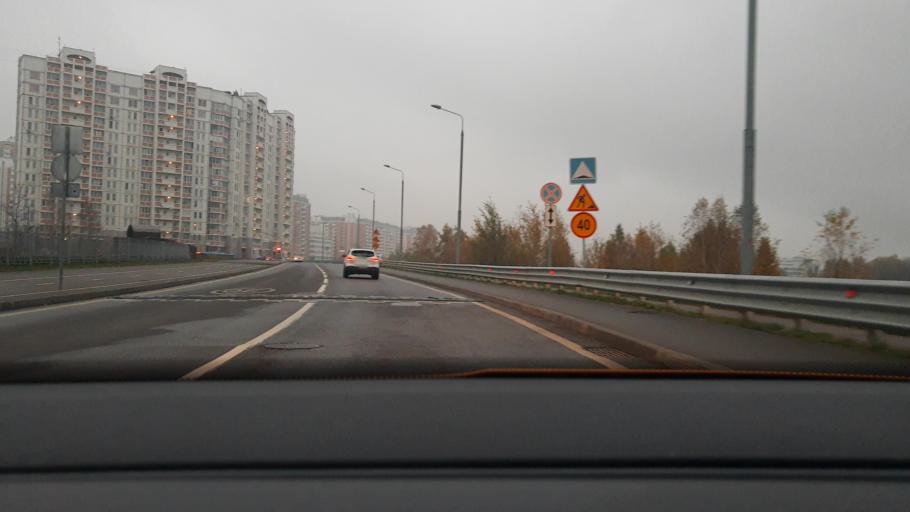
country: RU
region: Moscow
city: Severnyy
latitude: 55.9286
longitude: 37.5388
